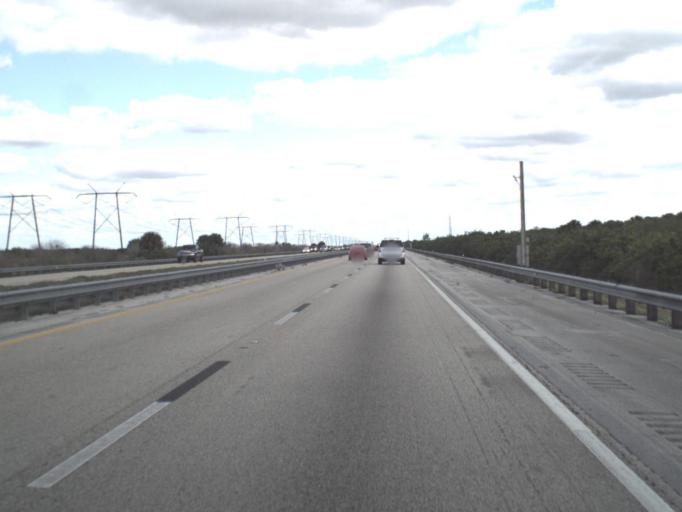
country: US
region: Florida
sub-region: Indian River County
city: Fellsmere
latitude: 27.5593
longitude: -80.7227
